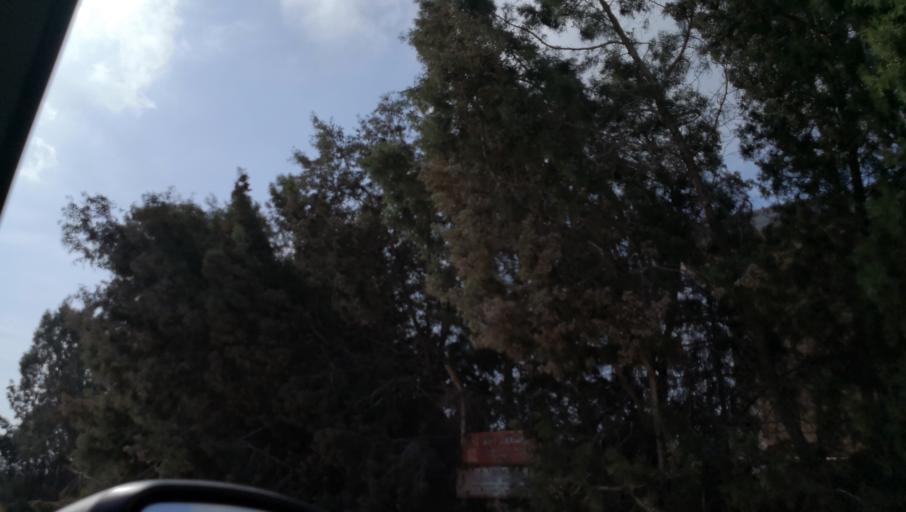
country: CY
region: Ammochostos
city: Protaras
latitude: 35.0140
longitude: 34.0320
